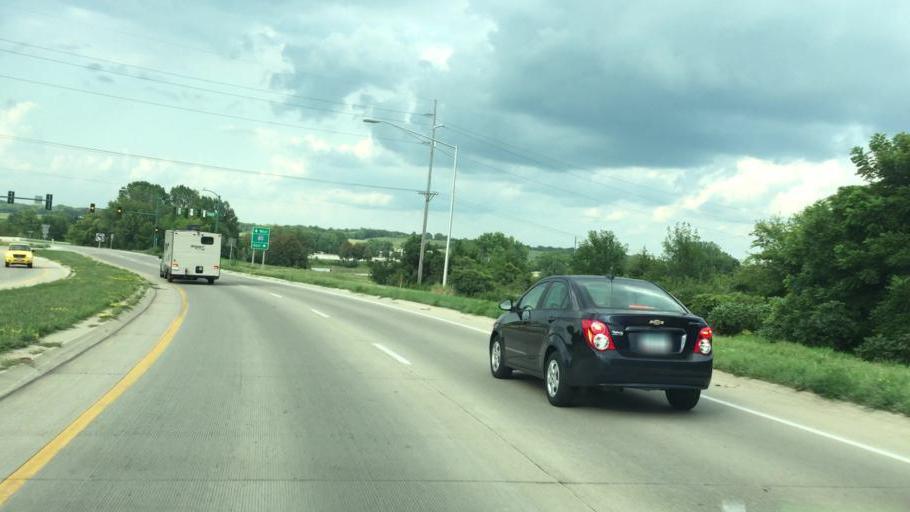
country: US
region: Iowa
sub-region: Johnson County
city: Iowa City
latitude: 41.6844
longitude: -91.5006
